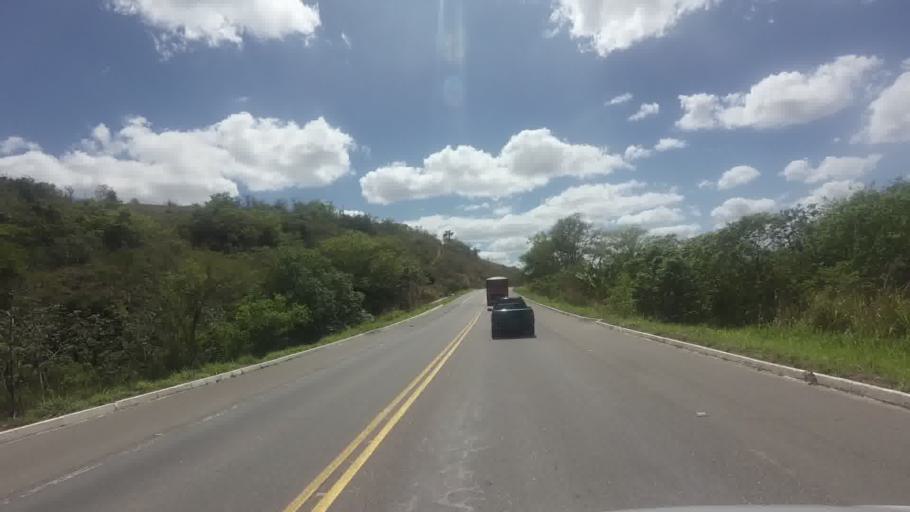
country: BR
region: Minas Gerais
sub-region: Recreio
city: Recreio
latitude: -21.6699
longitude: -42.3899
